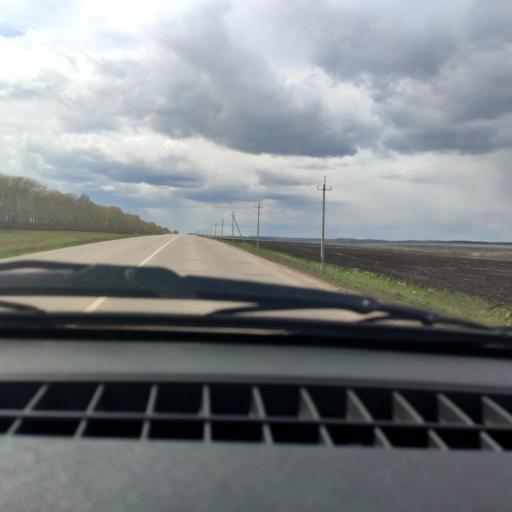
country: RU
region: Bashkortostan
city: Chekmagush
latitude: 55.1126
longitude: 54.8974
